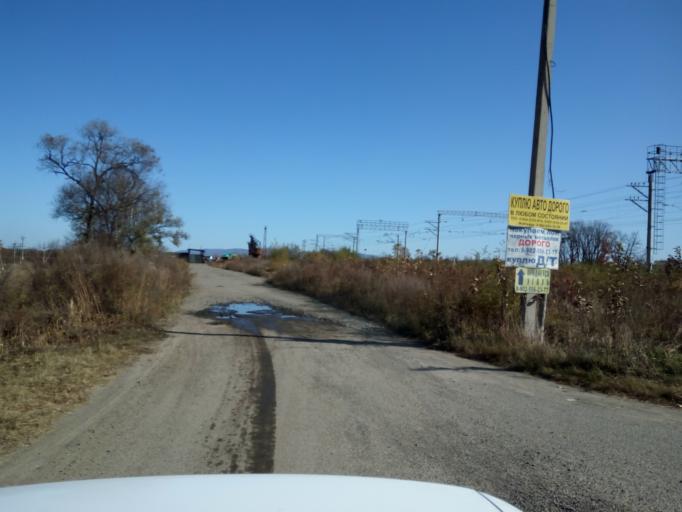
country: RU
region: Primorskiy
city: Dal'nerechensk
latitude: 45.9124
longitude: 133.7939
